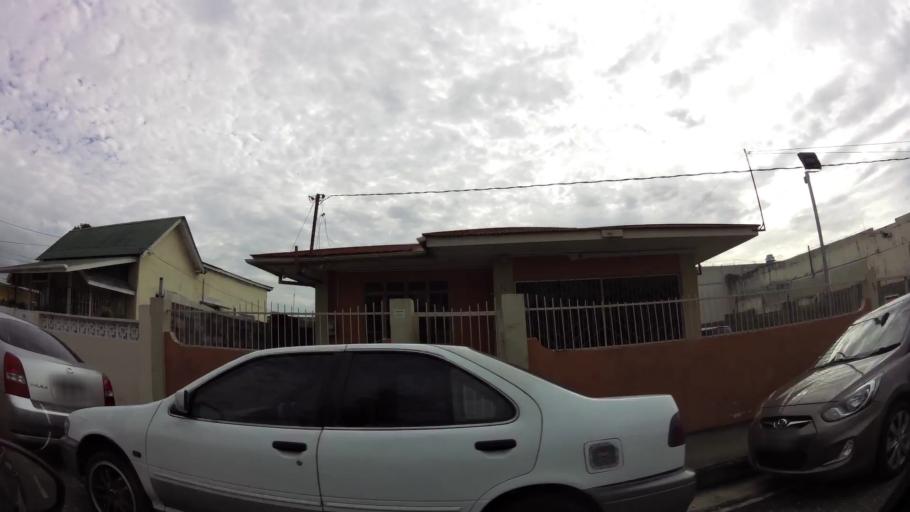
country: TT
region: City of Port of Spain
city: Port-of-Spain
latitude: 10.6615
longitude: -61.5192
